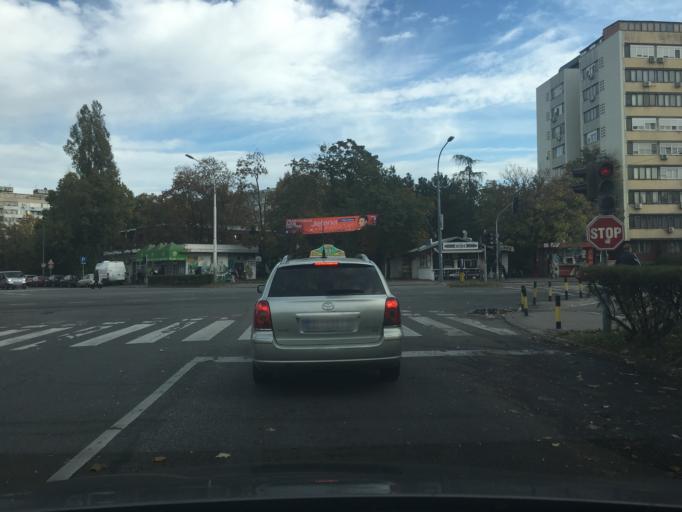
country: RS
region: Central Serbia
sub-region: Belgrade
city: Zemun
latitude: 44.8258
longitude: 20.4085
